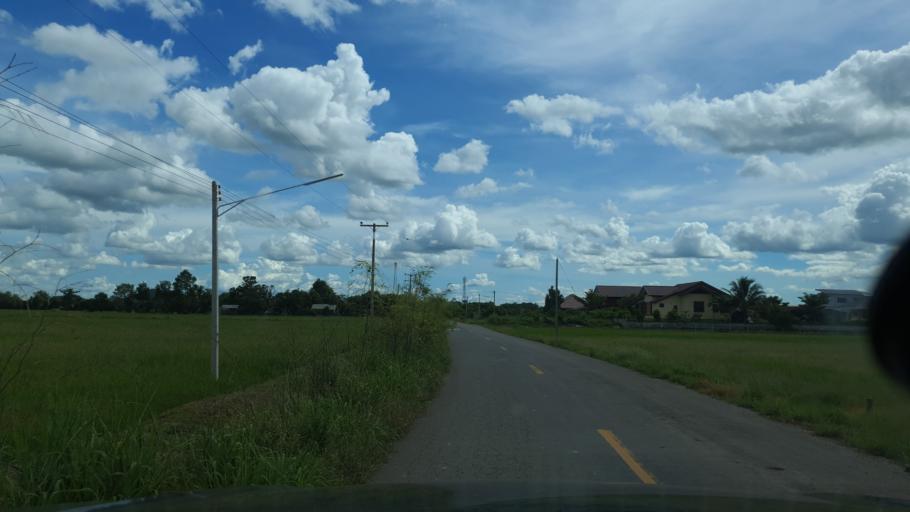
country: TH
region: Sukhothai
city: Thung Saliam
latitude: 17.3364
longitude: 99.6328
